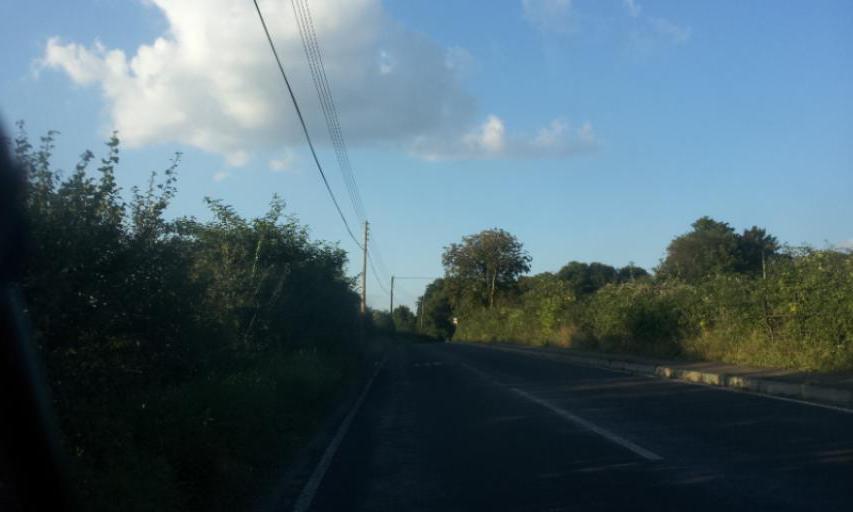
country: GB
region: England
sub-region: Medway
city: Halling
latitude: 51.3575
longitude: 0.4591
